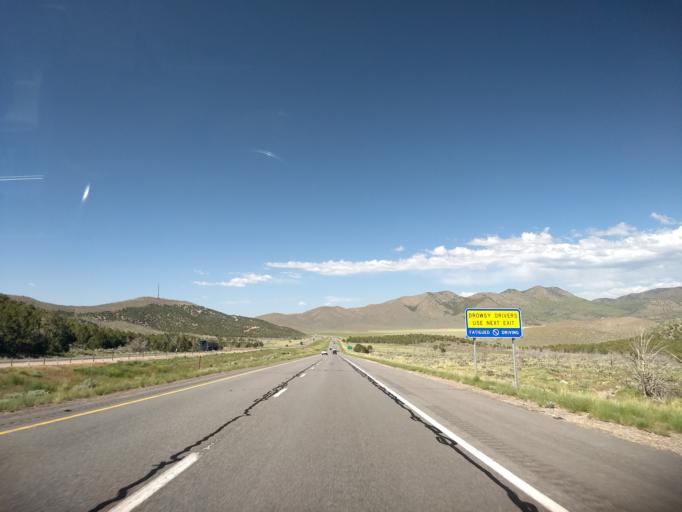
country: US
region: Utah
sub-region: Beaver County
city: Beaver
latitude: 38.6458
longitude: -112.6032
